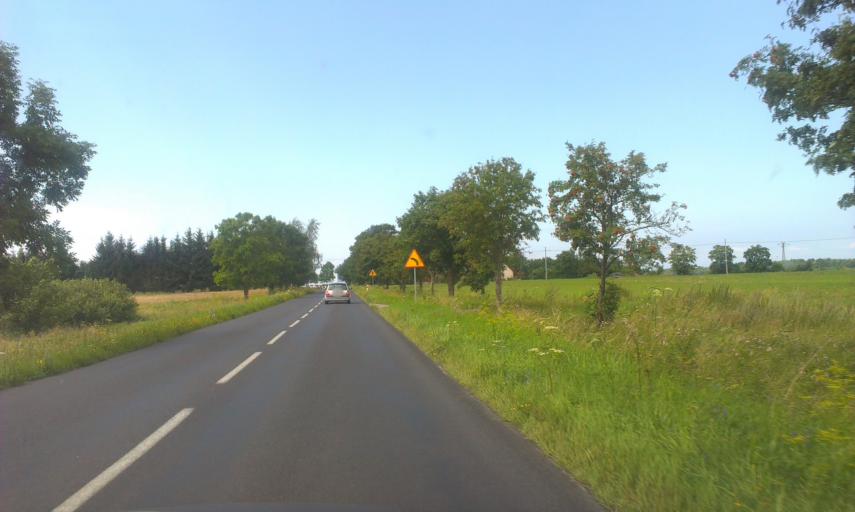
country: PL
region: West Pomeranian Voivodeship
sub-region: Powiat kolobrzeski
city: Kolobrzeg
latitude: 54.1513
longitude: 15.6351
